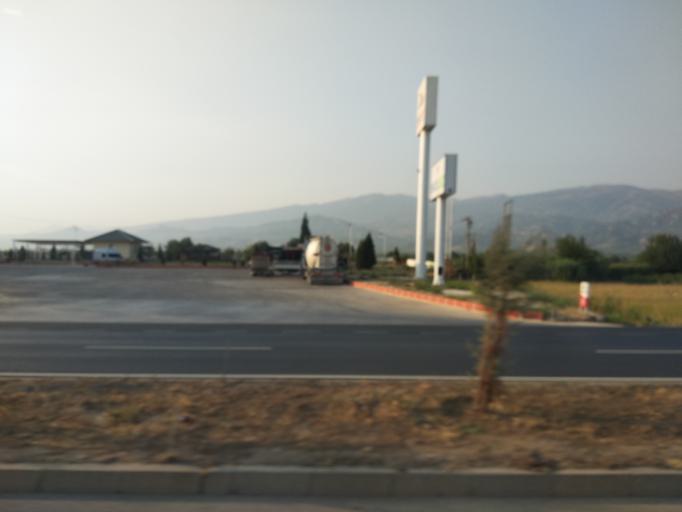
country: TR
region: Manisa
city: Salihli
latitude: 38.4972
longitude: 28.1906
